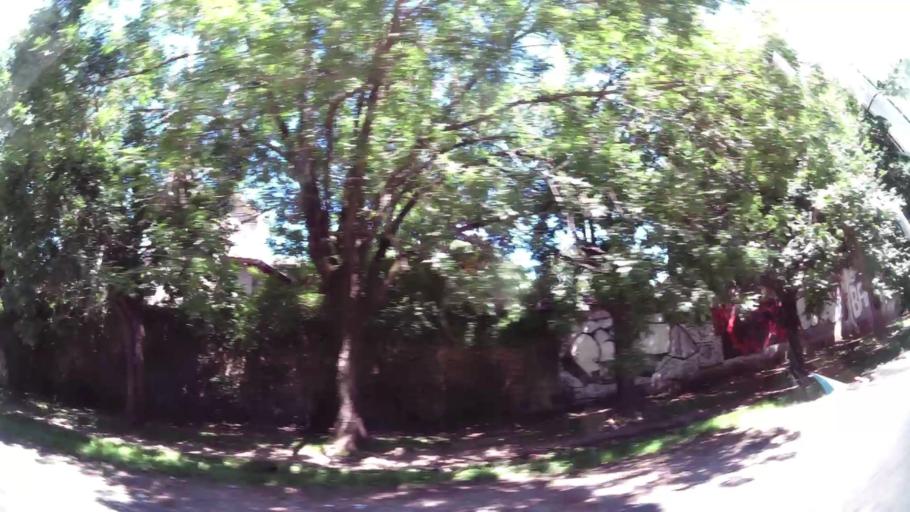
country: AR
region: Buenos Aires
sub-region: Partido de Tigre
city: Tigre
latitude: -34.4912
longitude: -58.6426
